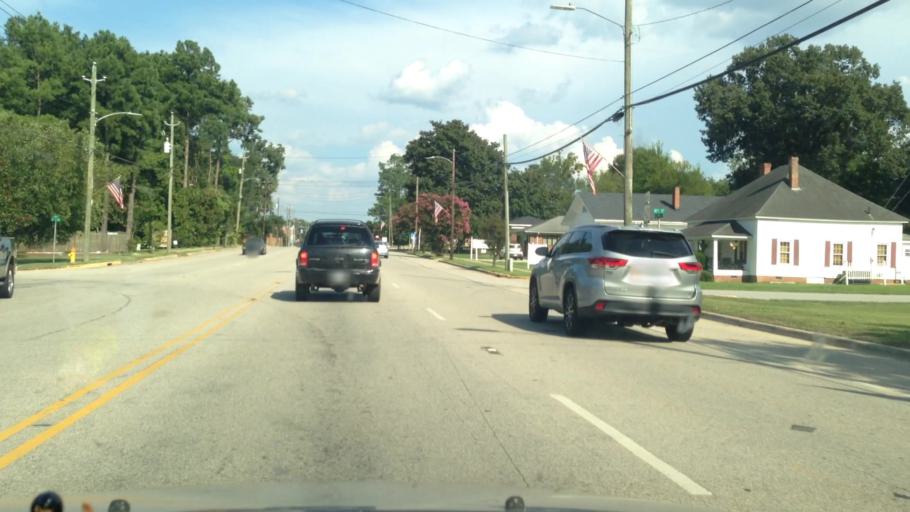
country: US
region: North Carolina
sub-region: Harnett County
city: Lillington
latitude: 35.3999
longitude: -78.8205
